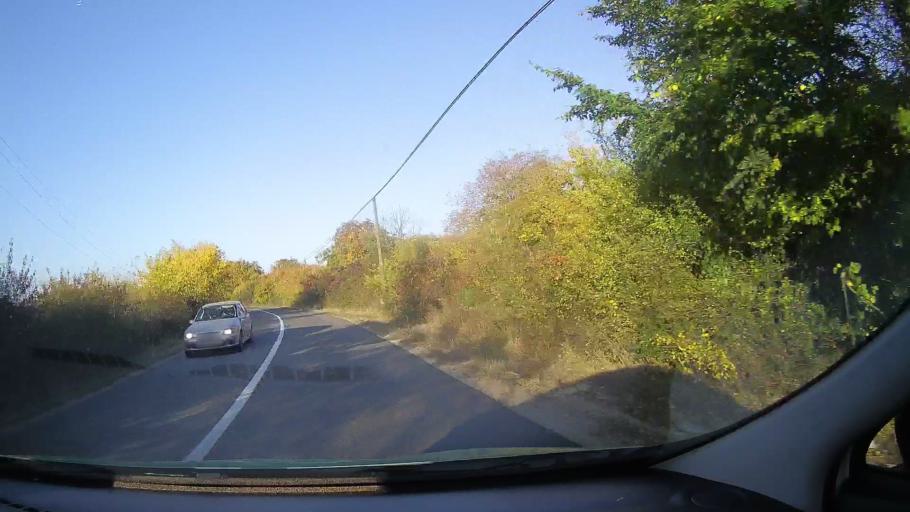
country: RO
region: Bihor
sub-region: Comuna Paleu
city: Paleu
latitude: 47.1023
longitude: 21.9282
